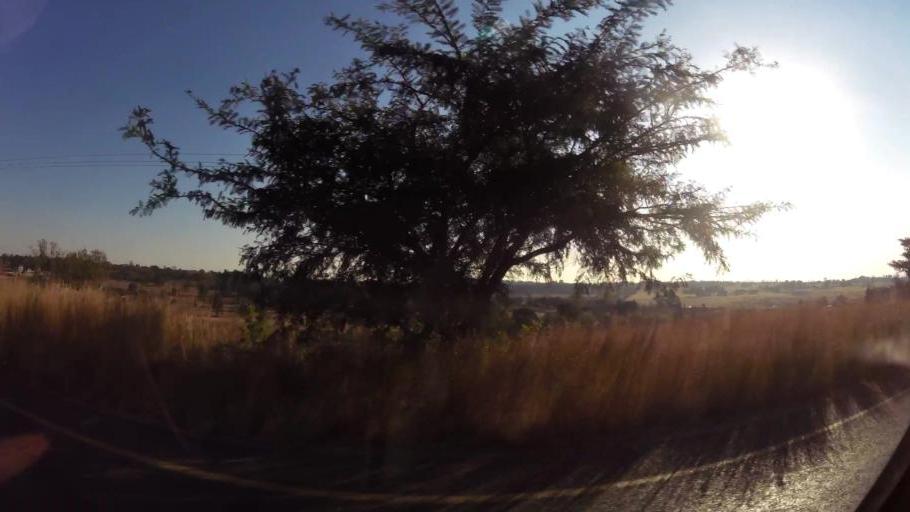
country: ZA
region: Gauteng
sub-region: West Rand District Municipality
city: Muldersdriseloop
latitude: -26.0315
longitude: 27.9091
